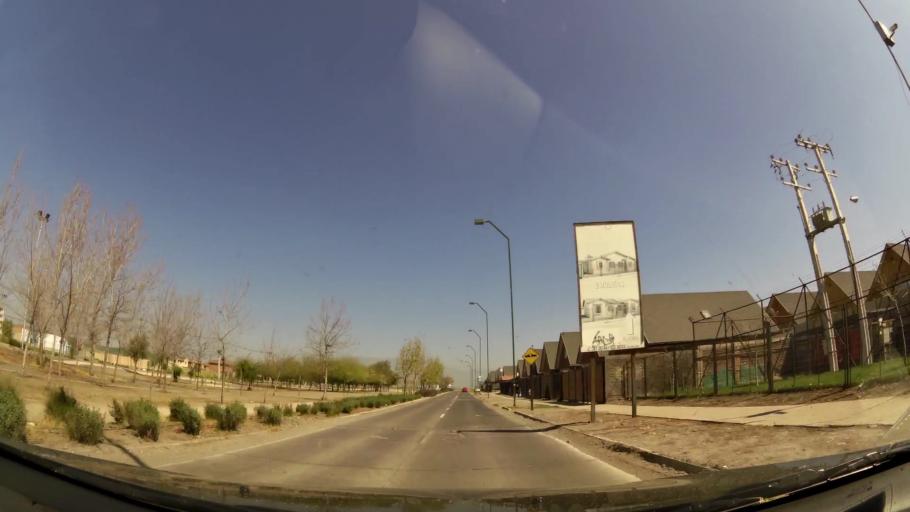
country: CL
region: Santiago Metropolitan
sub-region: Provincia de Chacabuco
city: Chicureo Abajo
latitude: -33.3287
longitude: -70.7622
